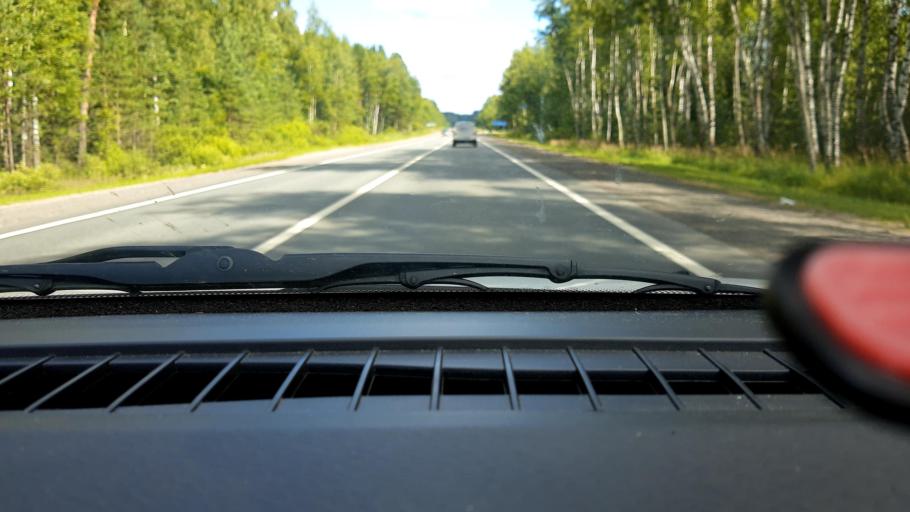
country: RU
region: Nizjnij Novgorod
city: Arzamas
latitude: 55.4860
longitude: 43.8873
